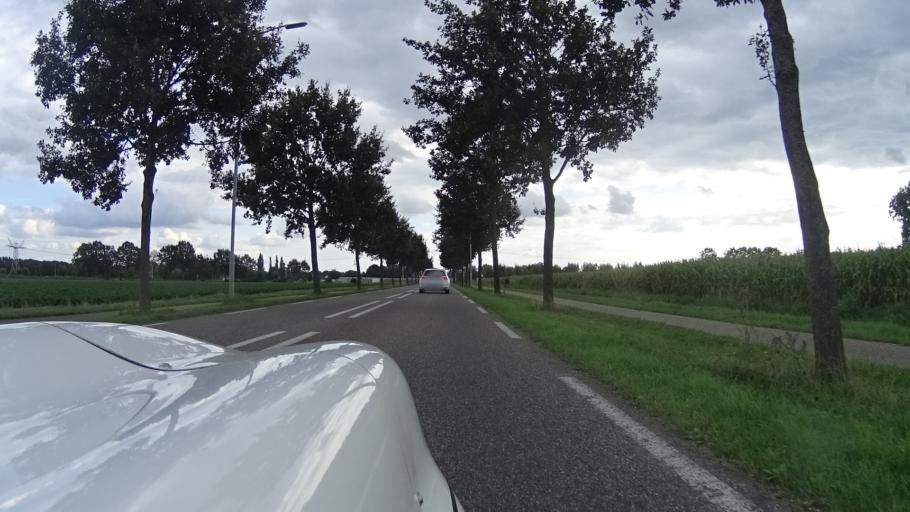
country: NL
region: North Brabant
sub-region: Gemeente Heusden
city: Heusden
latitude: 51.7143
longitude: 5.1822
